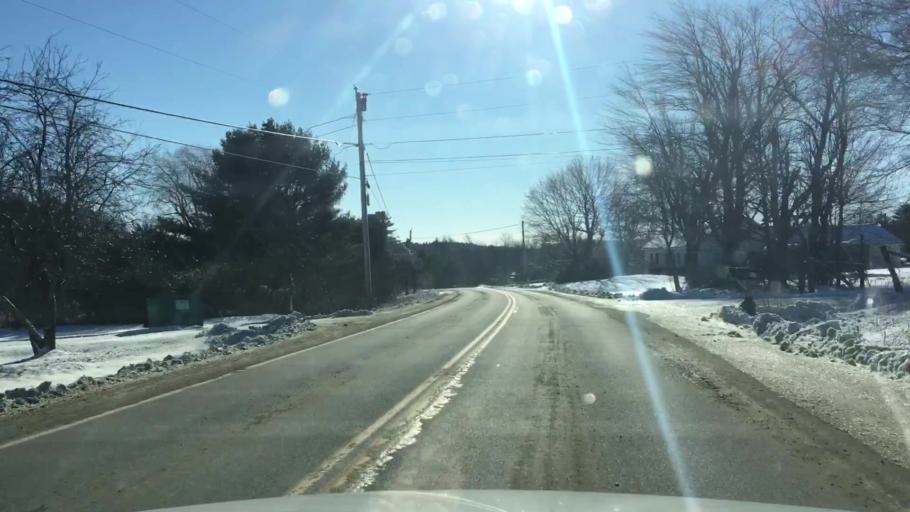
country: US
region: Maine
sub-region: Kennebec County
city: Readfield
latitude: 44.3620
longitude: -69.9900
